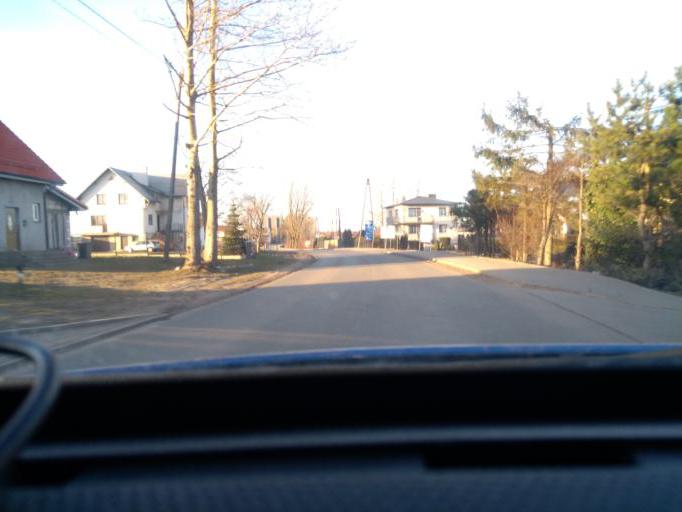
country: PL
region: Pomeranian Voivodeship
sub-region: Powiat kartuski
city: Przodkowo
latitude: 54.3822
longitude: 18.2883
